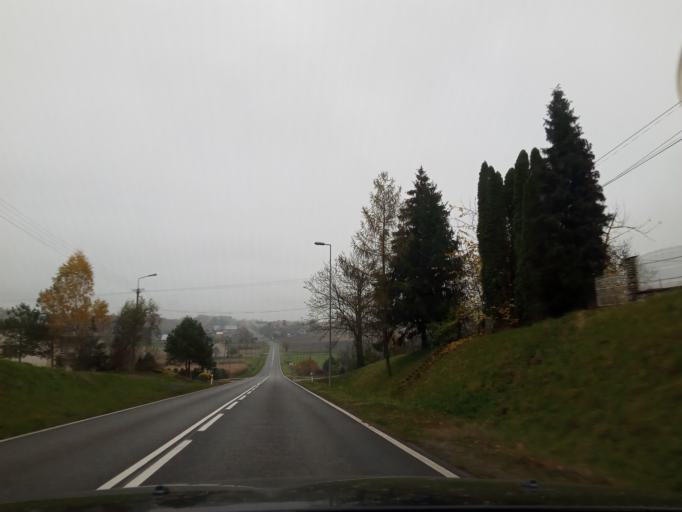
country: PL
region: Lesser Poland Voivodeship
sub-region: Powiat proszowicki
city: Klimontow
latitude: 50.2278
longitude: 20.3342
